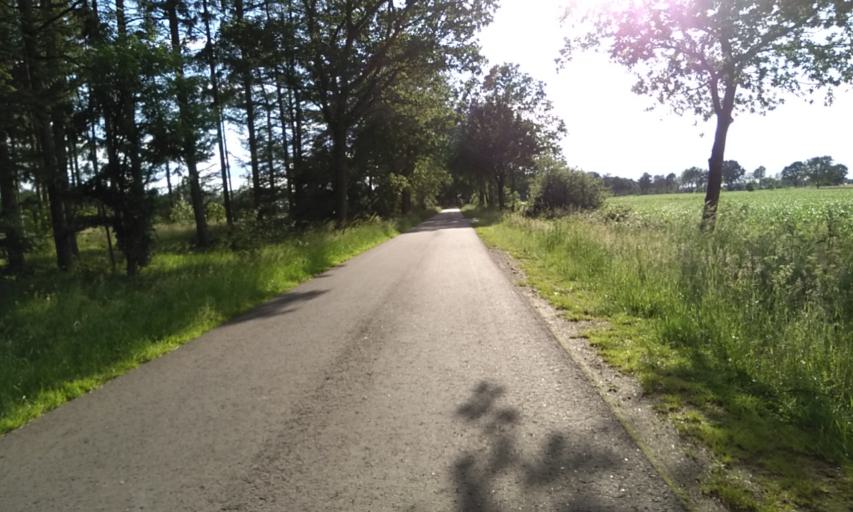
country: DE
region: Lower Saxony
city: Ahlerstedt
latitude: 53.3613
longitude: 9.4418
